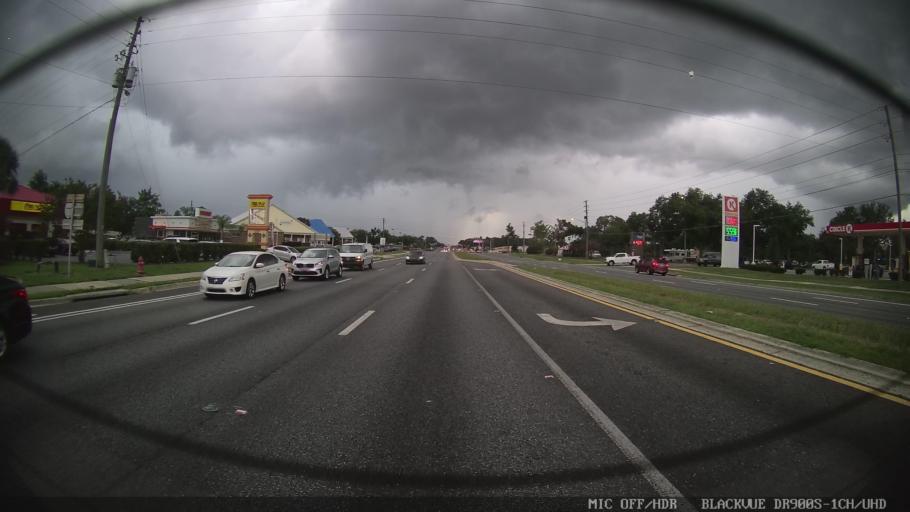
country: US
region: Florida
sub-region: Marion County
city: Ocala
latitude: 29.1482
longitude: -82.1884
